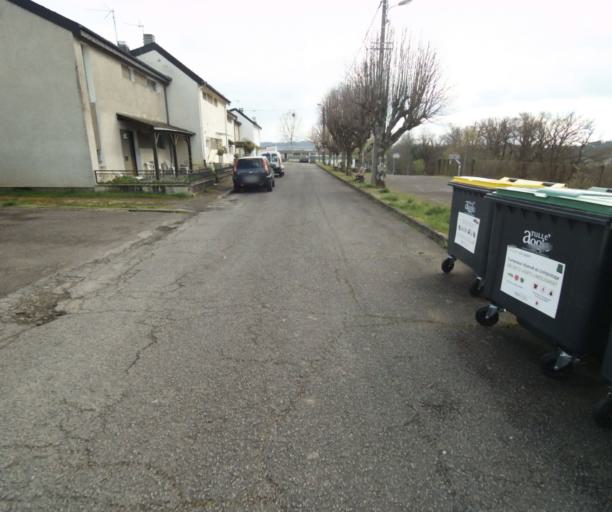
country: FR
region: Limousin
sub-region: Departement de la Correze
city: Tulle
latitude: 45.2574
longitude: 1.7391
